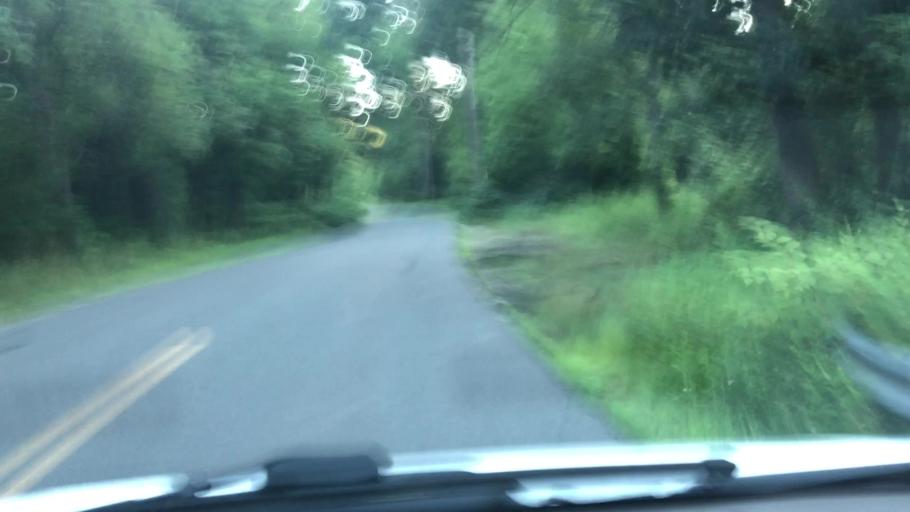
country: US
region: Massachusetts
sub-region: Hampshire County
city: Southampton
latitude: 42.2422
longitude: -72.7062
